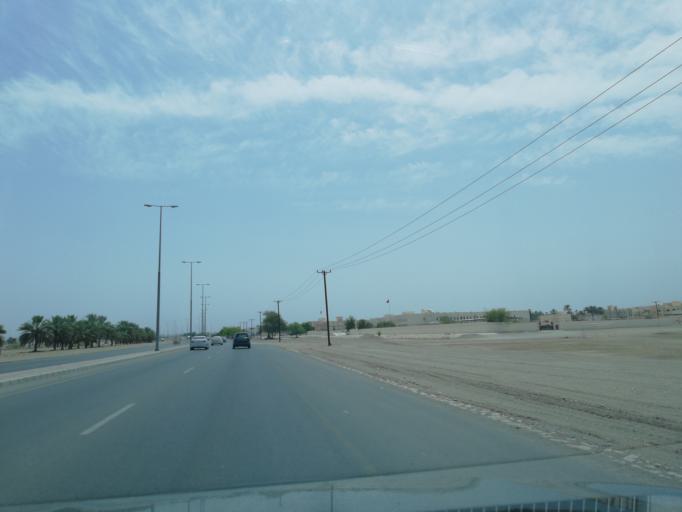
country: OM
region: Muhafazat Masqat
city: As Sib al Jadidah
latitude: 23.6737
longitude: 58.1647
